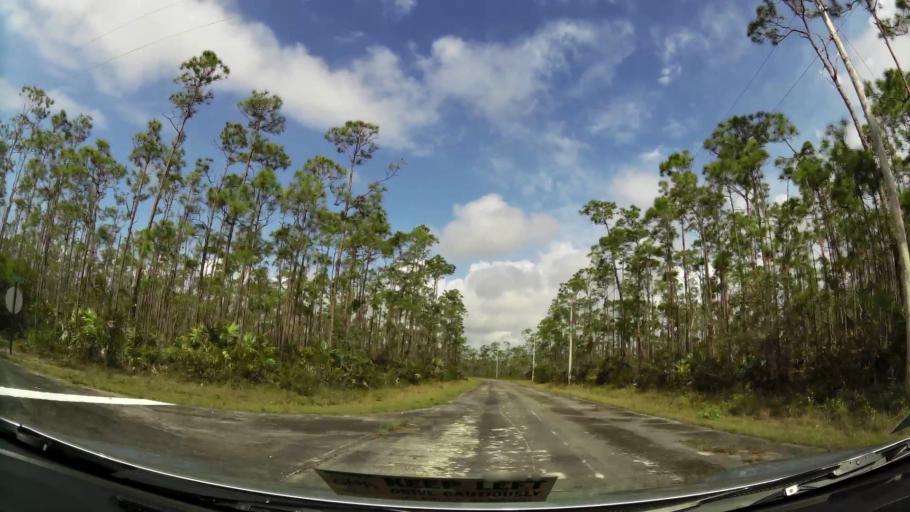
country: BS
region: Freeport
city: Lucaya
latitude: 26.5795
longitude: -78.5528
